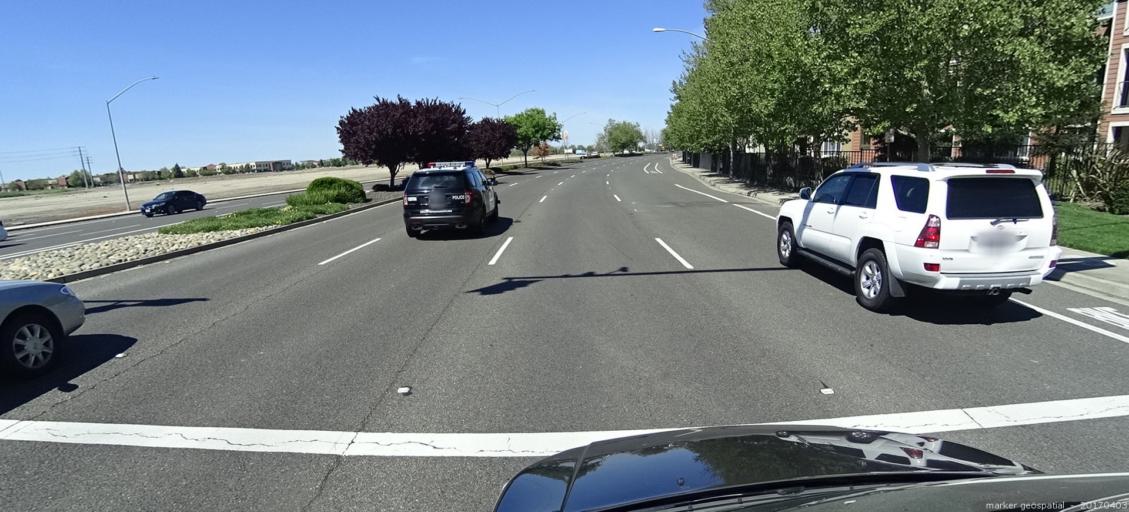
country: US
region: California
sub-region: Sacramento County
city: Sacramento
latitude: 38.6521
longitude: -121.5115
